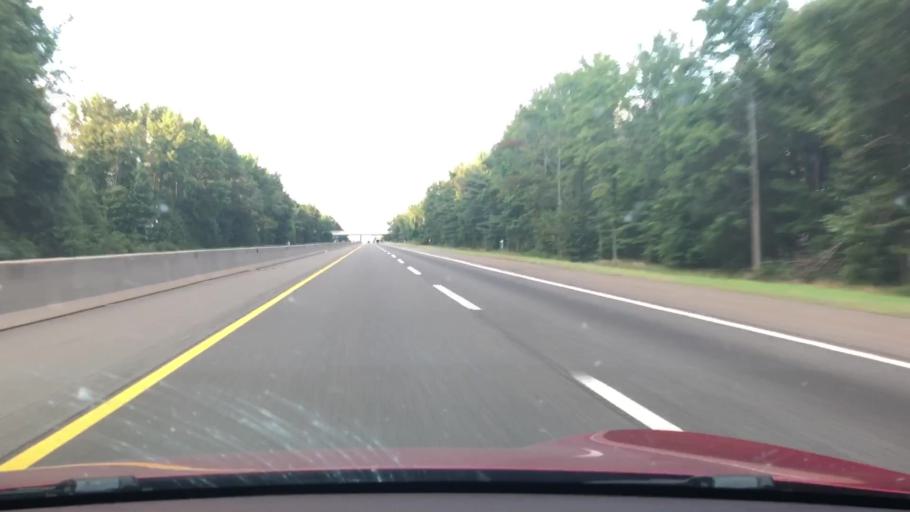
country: US
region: New Jersey
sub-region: Gloucester County
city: Mullica Hill
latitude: 39.7692
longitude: -75.2496
